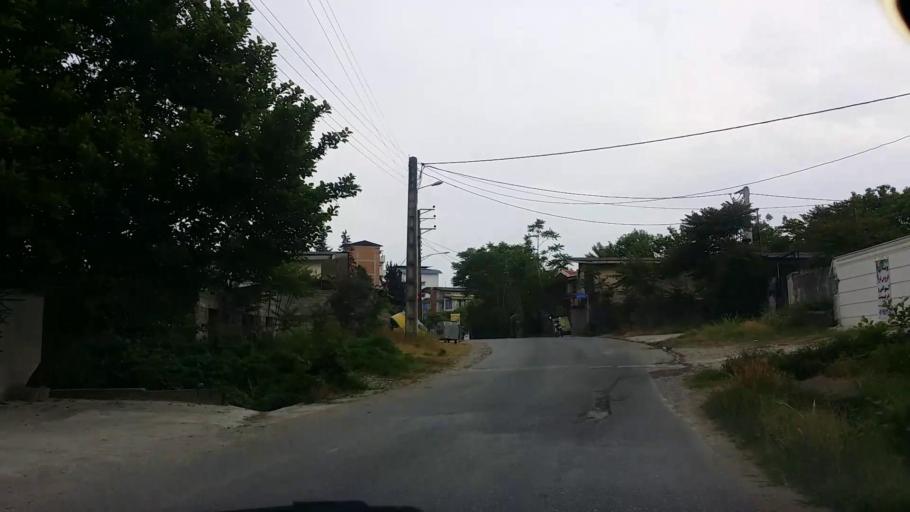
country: IR
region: Mazandaran
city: Chalus
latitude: 36.6858
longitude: 51.4143
